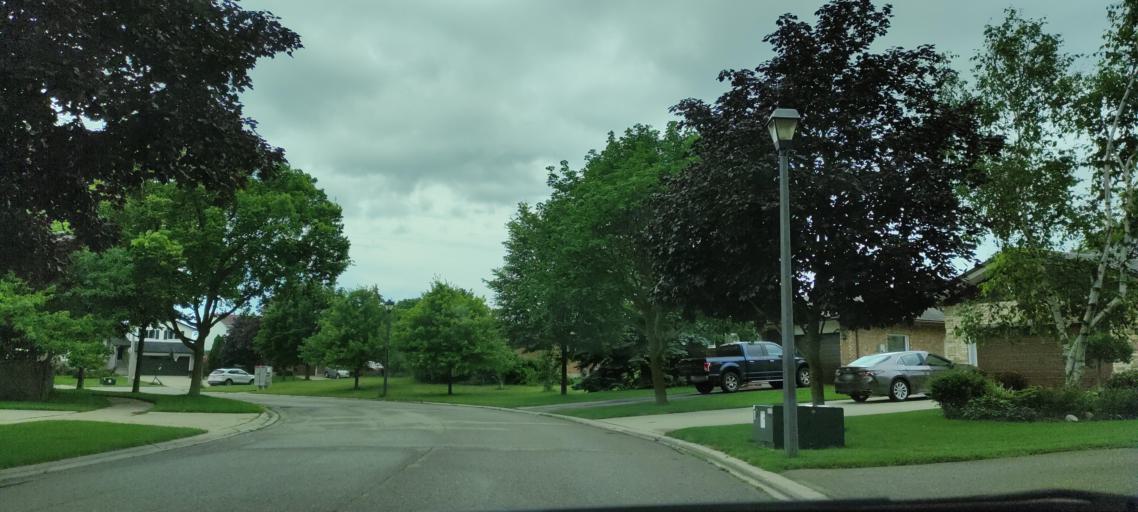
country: CA
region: Ontario
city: Stratford
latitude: 43.3846
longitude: -80.9816
